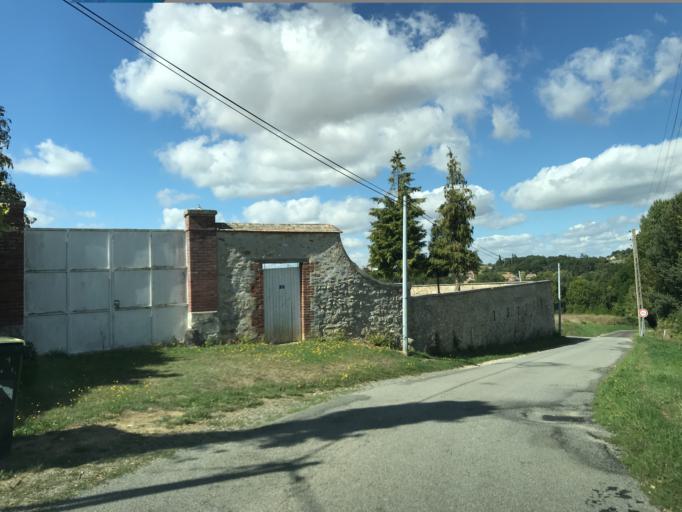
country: FR
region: Haute-Normandie
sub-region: Departement de l'Eure
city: La Chapelle-Reanville
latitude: 49.1076
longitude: 1.3864
